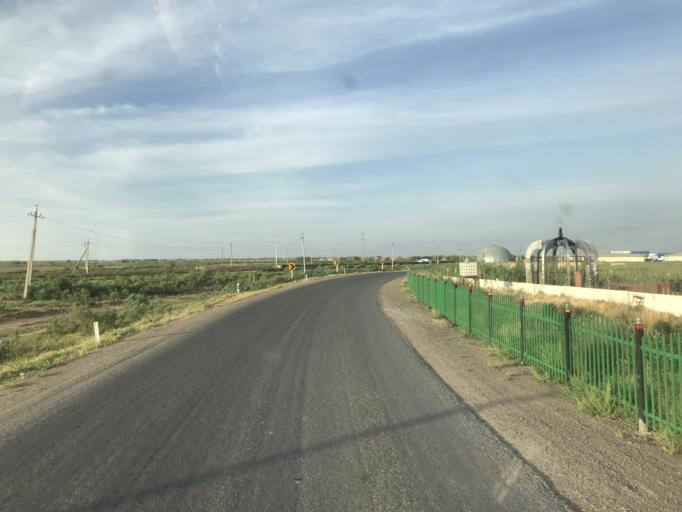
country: KZ
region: Ongtustik Qazaqstan
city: Asykata
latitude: 40.9068
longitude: 68.3673
